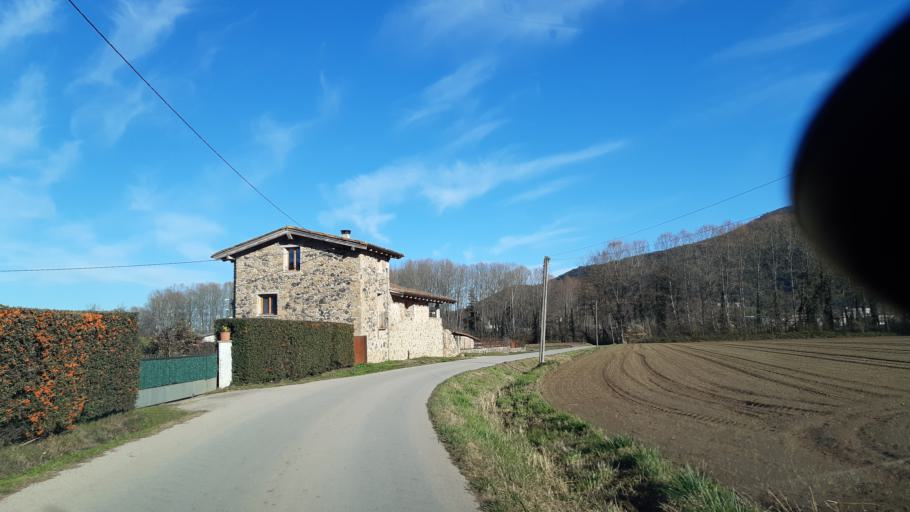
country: ES
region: Catalonia
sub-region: Provincia de Girona
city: Bas
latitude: 42.1427
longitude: 2.4472
